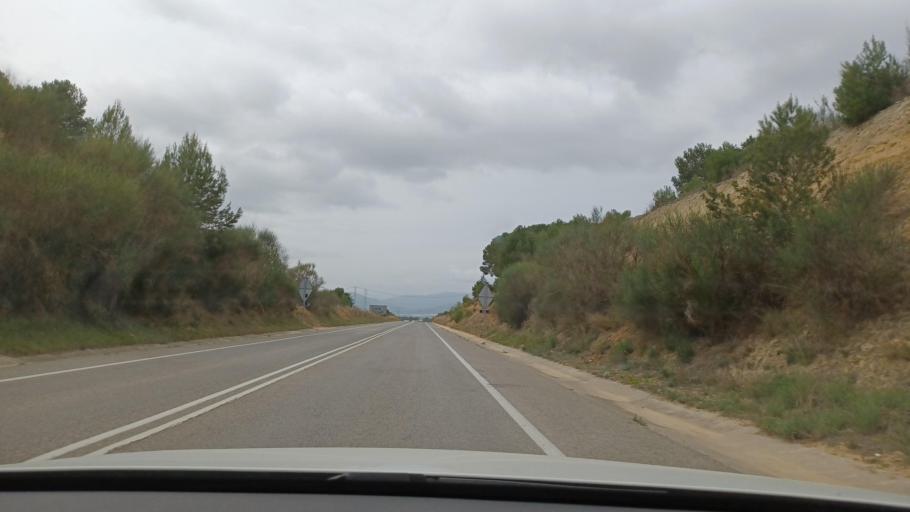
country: ES
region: Catalonia
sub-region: Provincia de Tarragona
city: La Secuita
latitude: 41.1966
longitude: 1.2601
